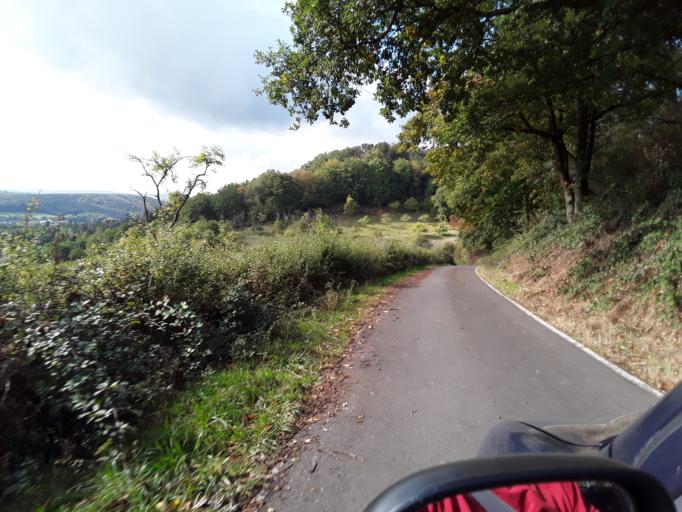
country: DE
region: Rheinland-Pfalz
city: Ramsen
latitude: 49.5532
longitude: 8.0200
